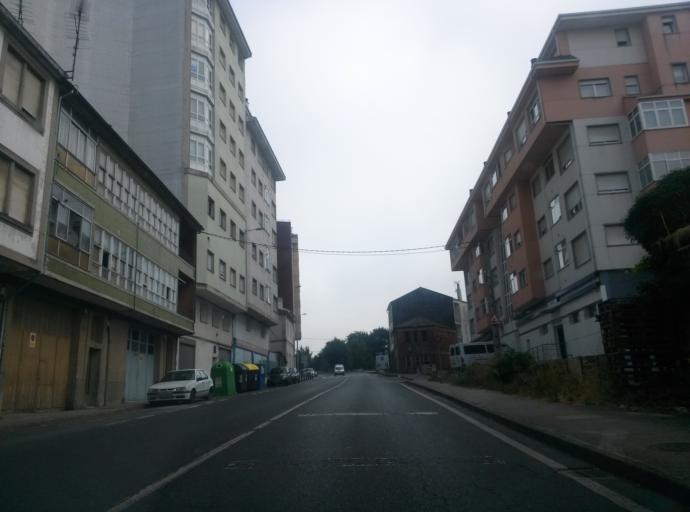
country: ES
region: Galicia
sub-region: Provincia de Lugo
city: Lugo
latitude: 43.0119
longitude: -7.5489
